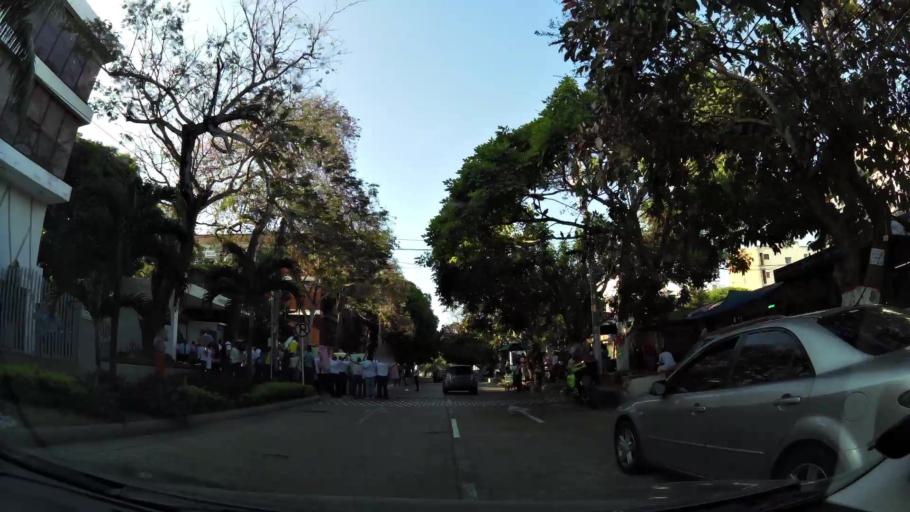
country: CO
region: Atlantico
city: Barranquilla
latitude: 11.0044
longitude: -74.8240
